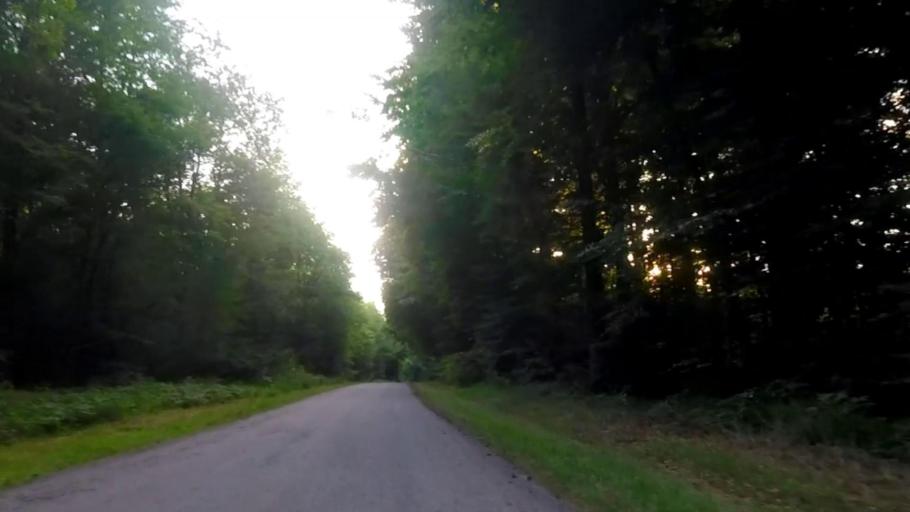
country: DE
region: Baden-Wuerttemberg
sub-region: Regierungsbezirk Stuttgart
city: Spiegelberg
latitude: 49.0131
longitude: 9.4107
